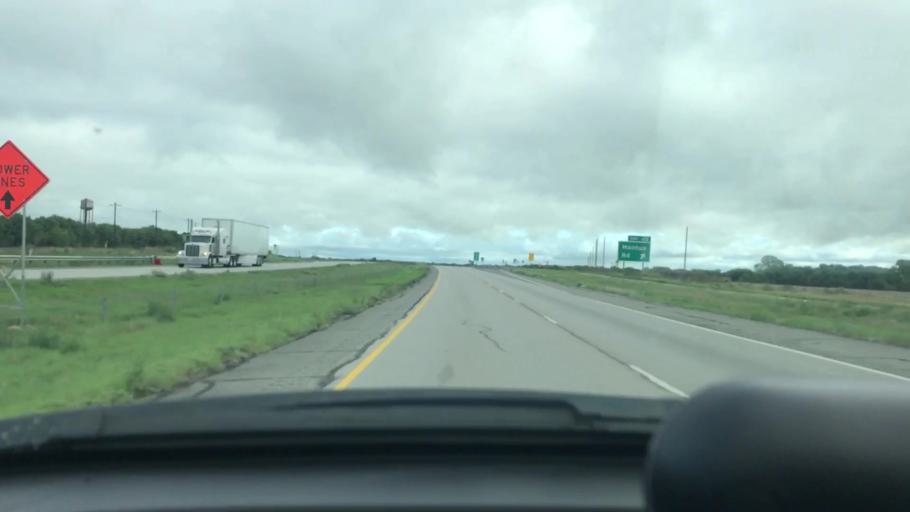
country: US
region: Texas
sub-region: Collin County
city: Anna
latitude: 33.3767
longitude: -96.5809
